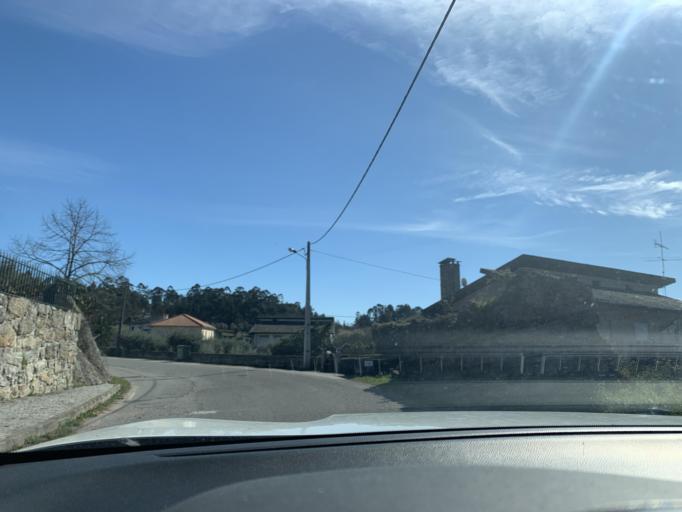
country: PT
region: Viseu
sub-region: Concelho de Tondela
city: Tondela
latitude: 40.5873
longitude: -8.0254
